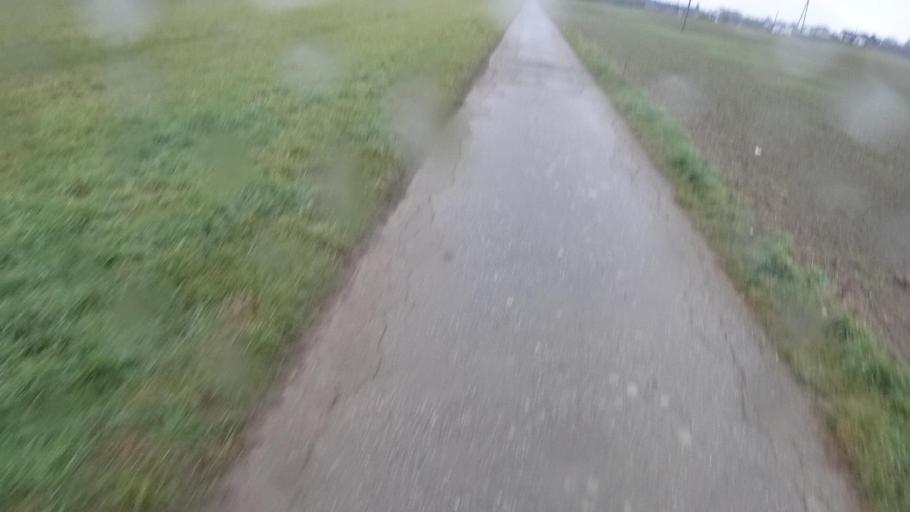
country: DE
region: Rheinland-Pfalz
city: Wiebelsheim
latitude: 50.0754
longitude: 7.6134
